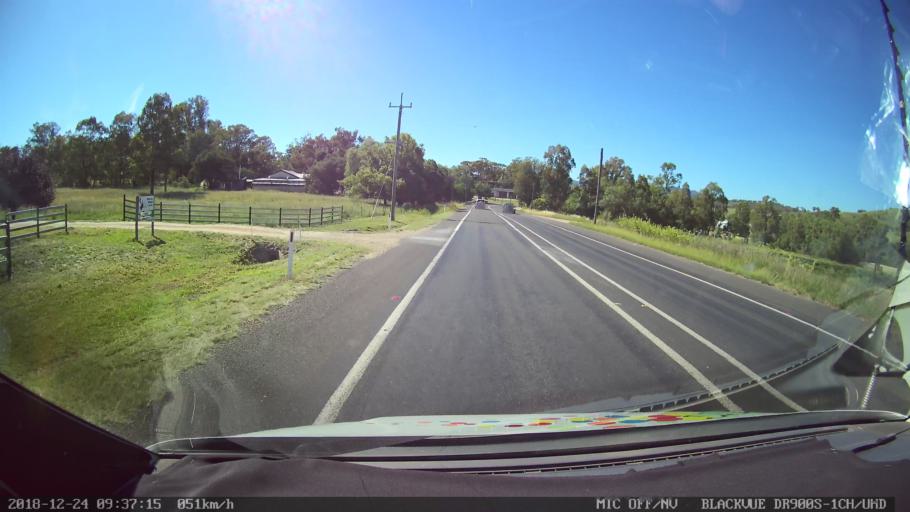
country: AU
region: New South Wales
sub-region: Liverpool Plains
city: Quirindi
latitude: -31.6437
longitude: 150.7250
